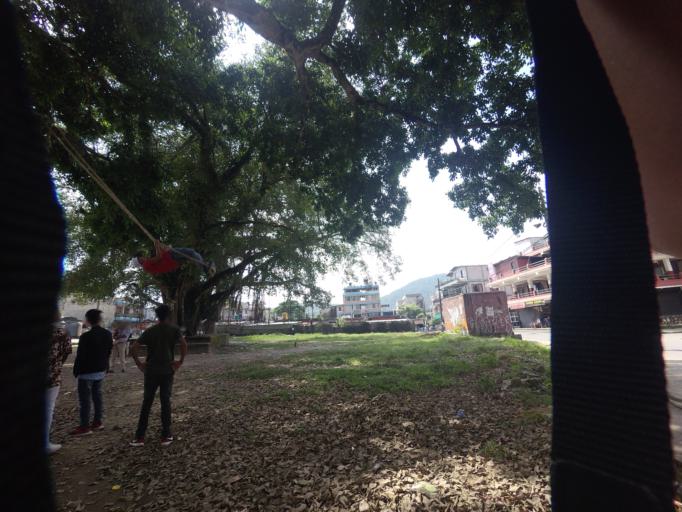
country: NP
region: Western Region
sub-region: Gandaki Zone
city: Pokhara
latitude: 28.2142
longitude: 83.9605
